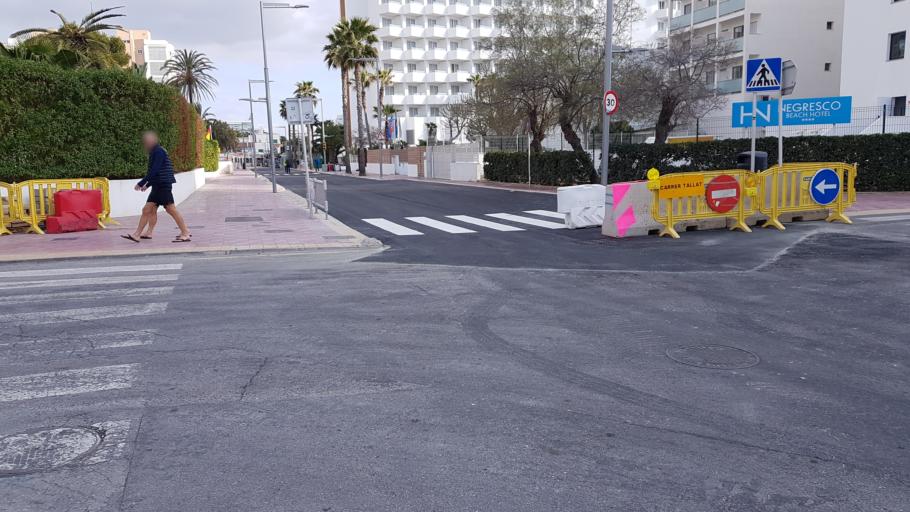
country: ES
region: Balearic Islands
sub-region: Illes Balears
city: s'Arenal
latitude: 39.5264
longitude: 2.7352
